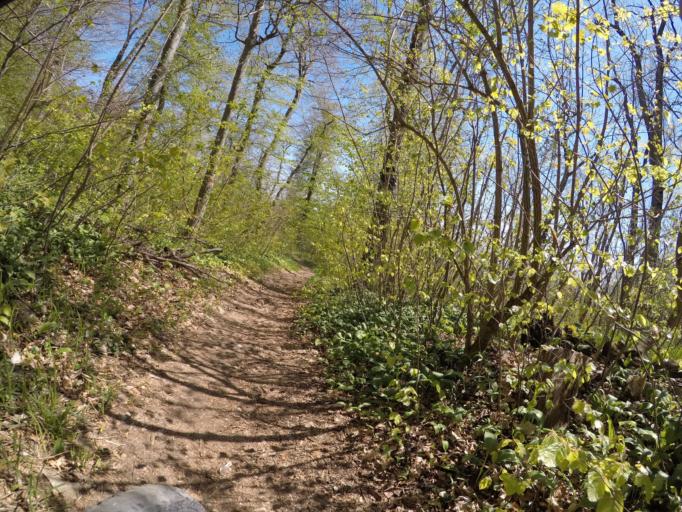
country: AT
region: Lower Austria
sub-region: Politischer Bezirk Modling
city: Gumpoldskirchen
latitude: 48.0508
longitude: 16.2531
